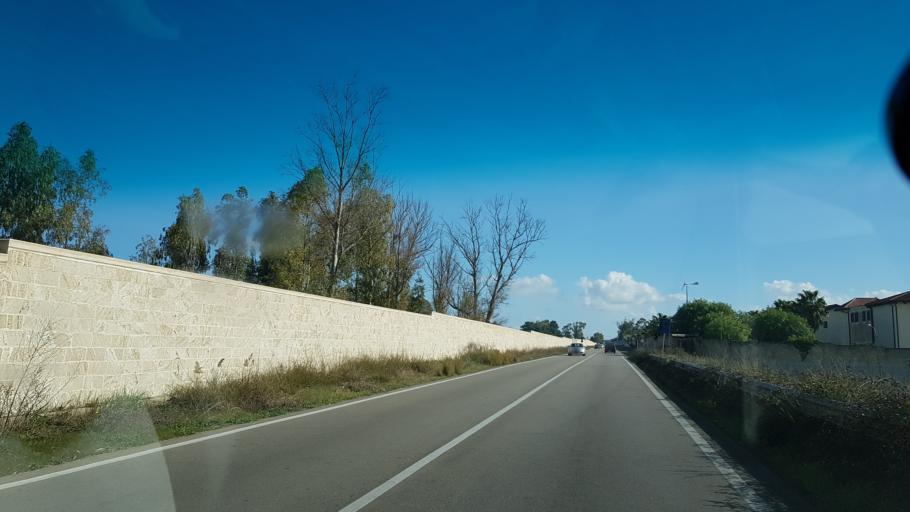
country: IT
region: Apulia
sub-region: Provincia di Lecce
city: Arnesano
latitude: 40.3587
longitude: 18.1149
